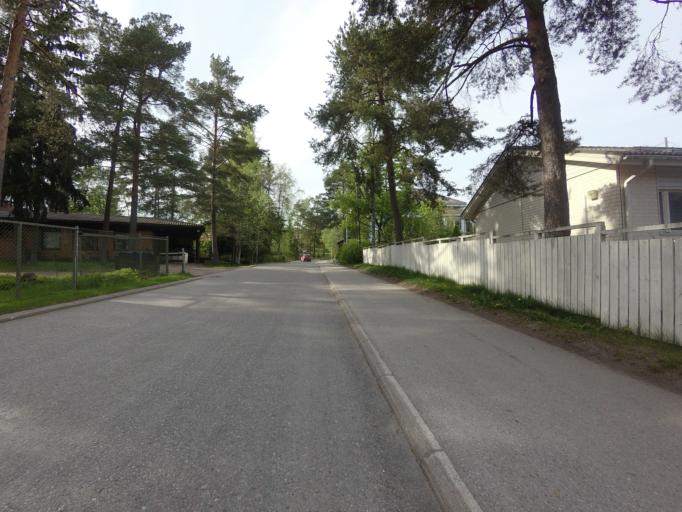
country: FI
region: Uusimaa
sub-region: Helsinki
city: Espoo
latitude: 60.1613
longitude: 24.6900
